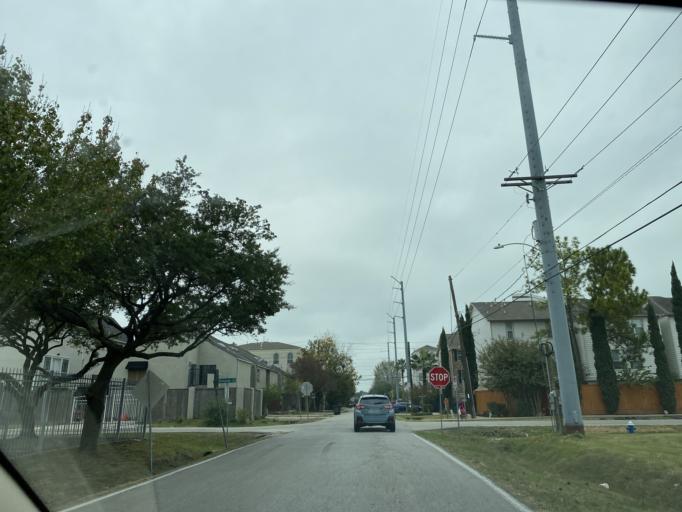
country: US
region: Texas
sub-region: Harris County
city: Bellaire
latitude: 29.7340
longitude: -95.4804
